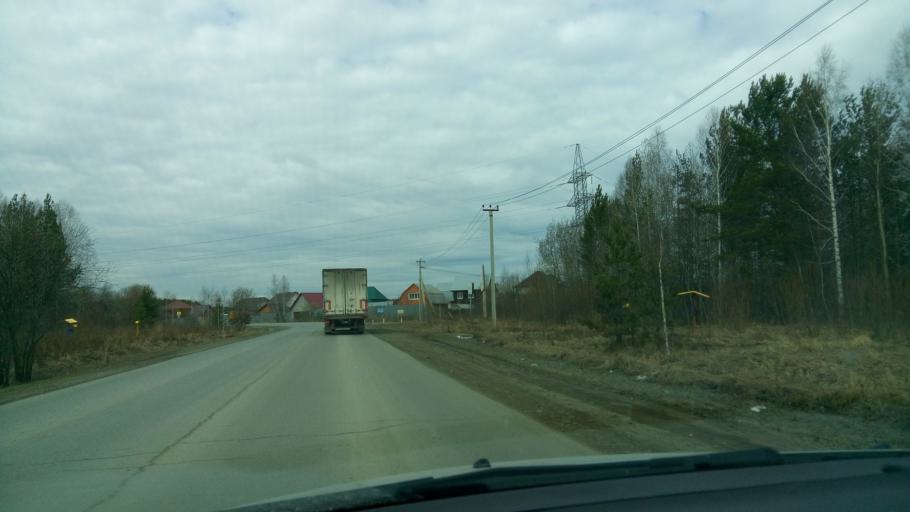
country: RU
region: Sverdlovsk
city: Verkhnyaya Pyshma
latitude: 56.9554
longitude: 60.6590
